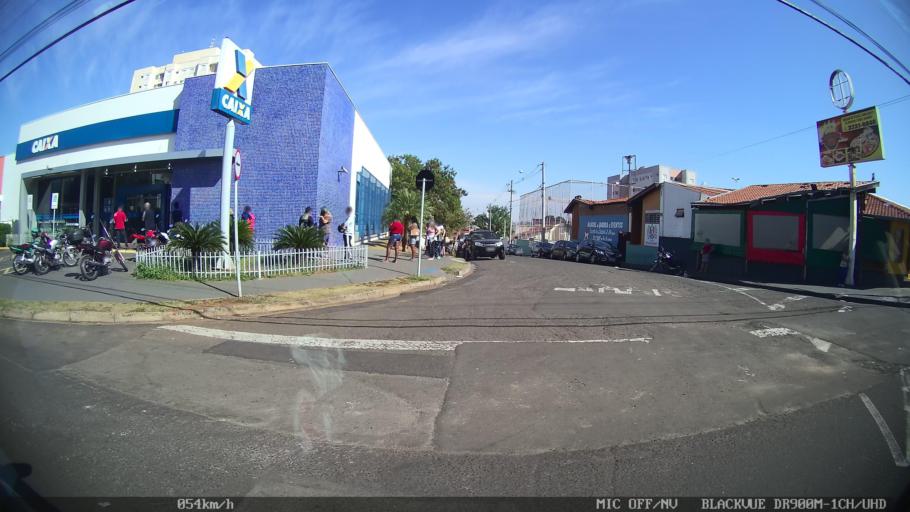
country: BR
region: Sao Paulo
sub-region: Sao Jose Do Rio Preto
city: Sao Jose do Rio Preto
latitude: -20.7846
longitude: -49.3687
